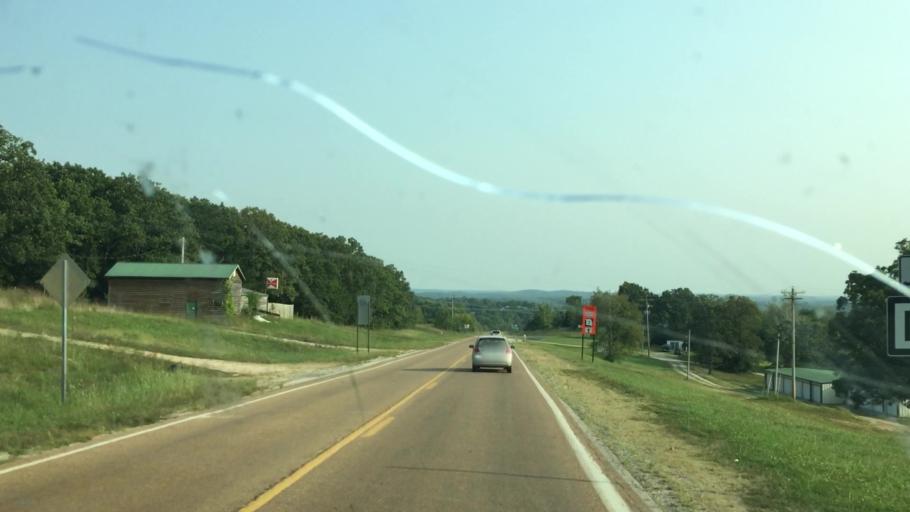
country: US
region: Missouri
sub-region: Pulaski County
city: Richland
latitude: 37.8437
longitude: -92.4106
